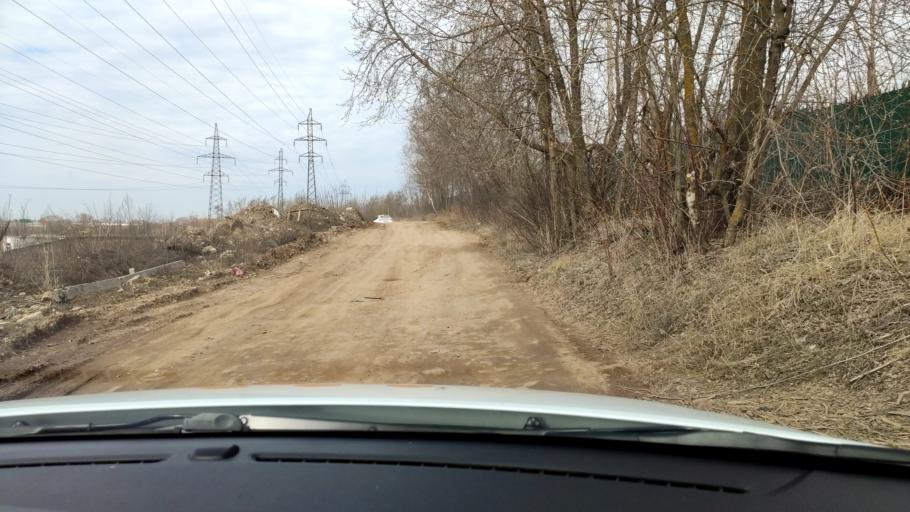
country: RU
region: Tatarstan
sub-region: Gorod Kazan'
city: Kazan
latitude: 55.8162
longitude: 49.2121
